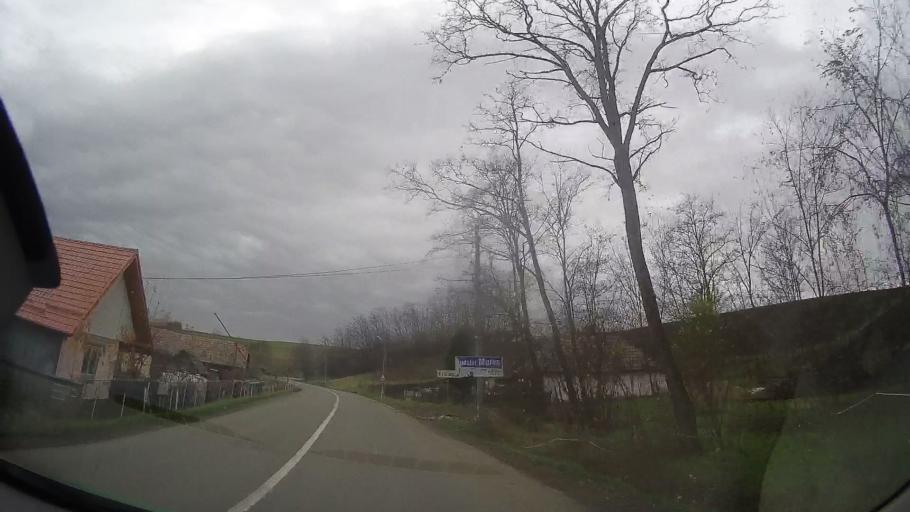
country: RO
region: Mures
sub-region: Comuna Craesti
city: Craiesti
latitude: 46.7732
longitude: 24.4251
